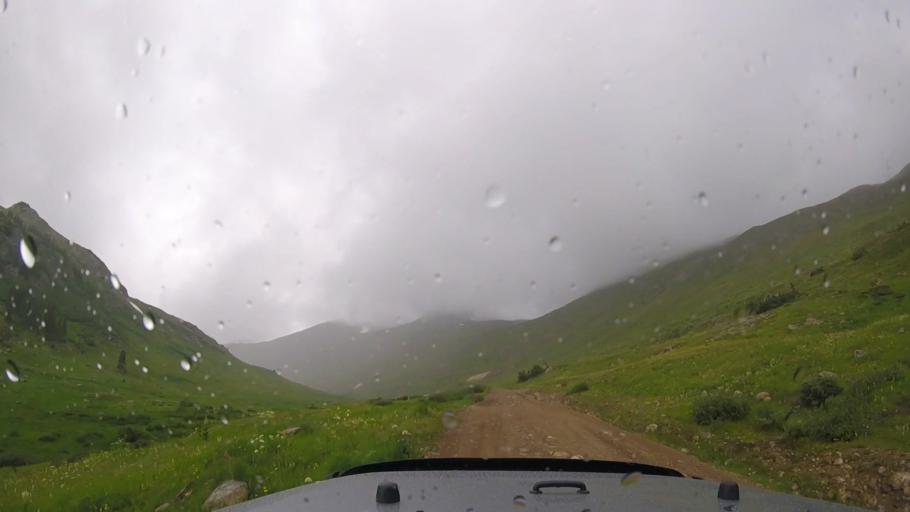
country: US
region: Colorado
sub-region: Ouray County
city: Ouray
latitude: 37.9320
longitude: -107.5906
